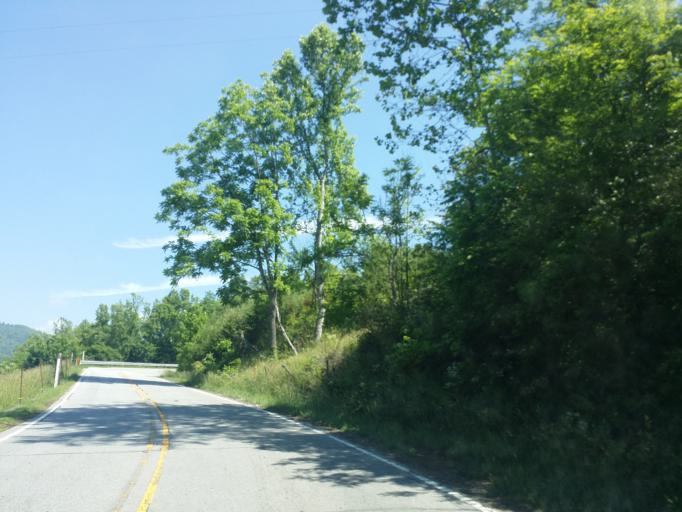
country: US
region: North Carolina
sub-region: Madison County
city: Marshall
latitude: 35.7030
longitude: -82.7484
